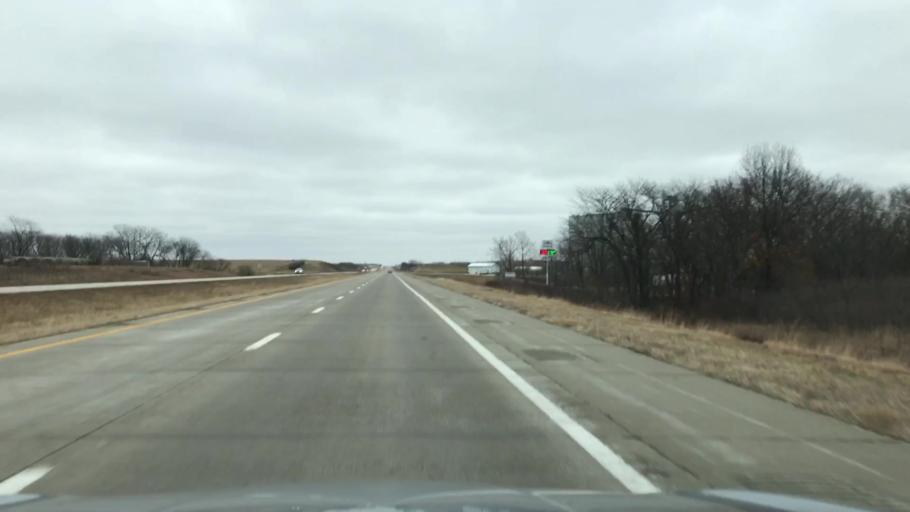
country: US
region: Missouri
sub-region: Caldwell County
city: Hamilton
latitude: 39.7353
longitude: -93.9127
